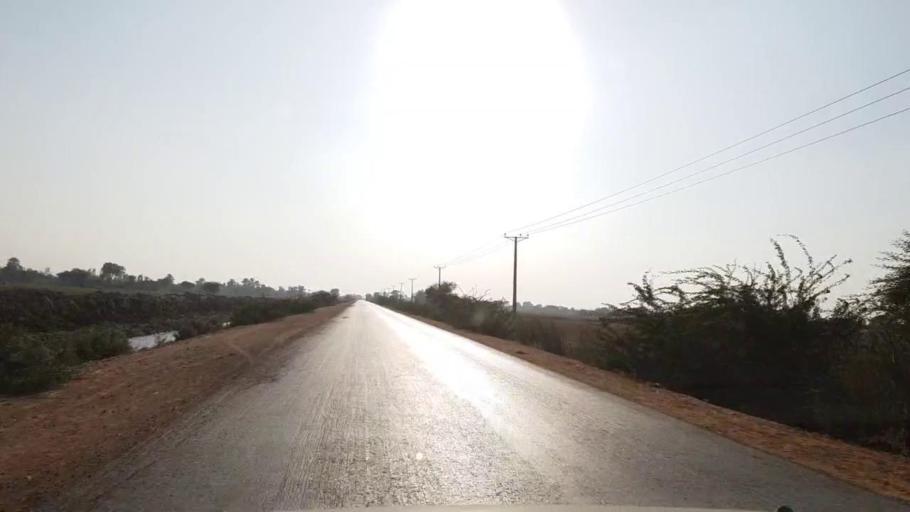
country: PK
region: Sindh
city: Mirpur Batoro
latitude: 24.7949
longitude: 68.3017
